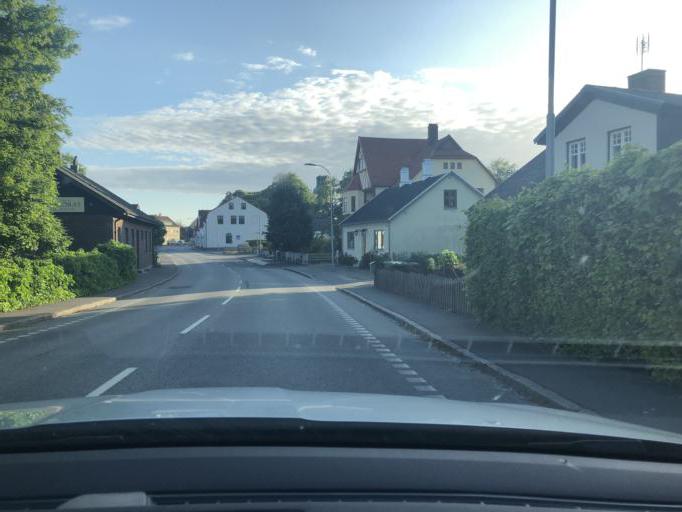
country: SE
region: Skane
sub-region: Simrishamns Kommun
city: Simrishamn
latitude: 55.4589
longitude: 14.1814
